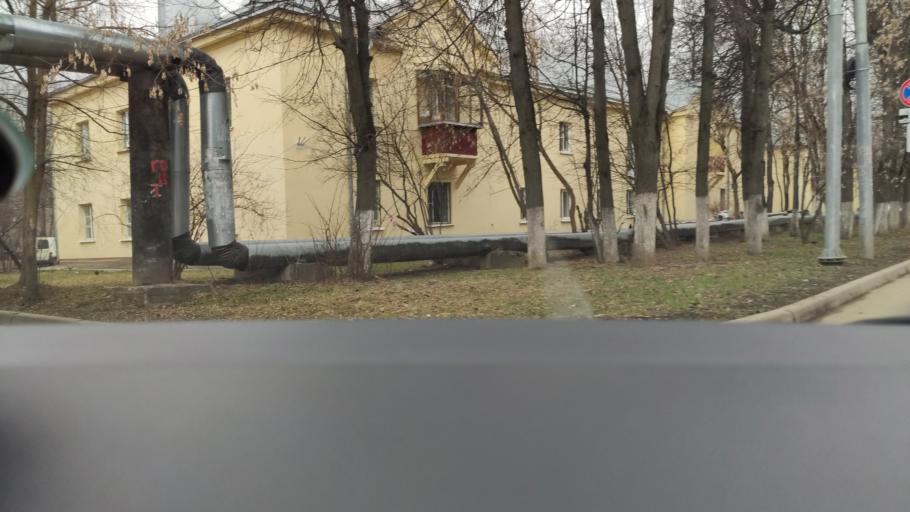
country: RU
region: Moskovskaya
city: Vatutinki
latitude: 55.5035
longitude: 37.3316
